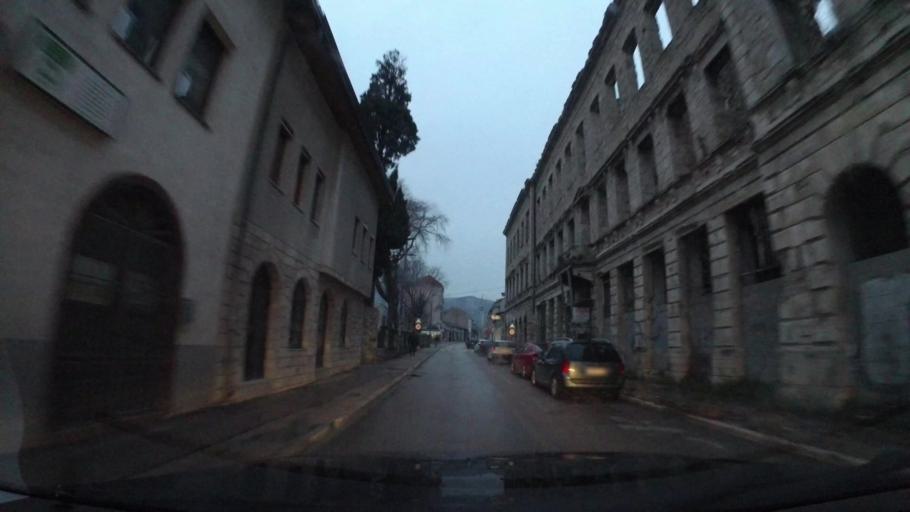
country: BA
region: Federation of Bosnia and Herzegovina
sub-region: Hercegovacko-Bosanski Kanton
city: Mostar
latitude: 43.3367
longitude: 17.8162
